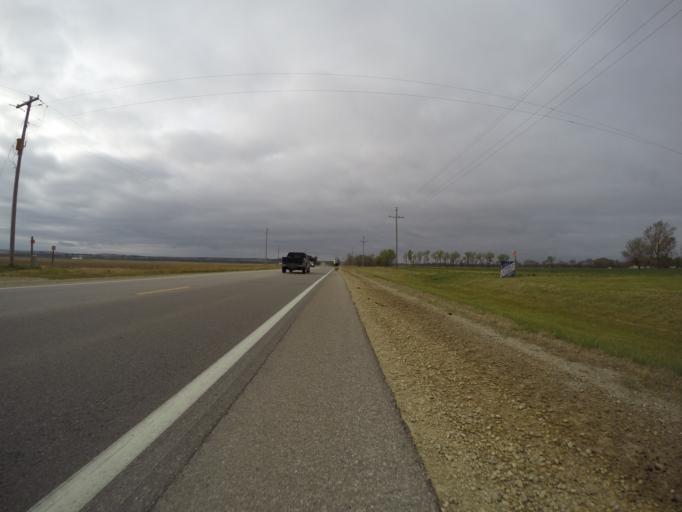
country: US
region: Kansas
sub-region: Pottawatomie County
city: Wamego
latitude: 39.1778
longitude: -96.3054
